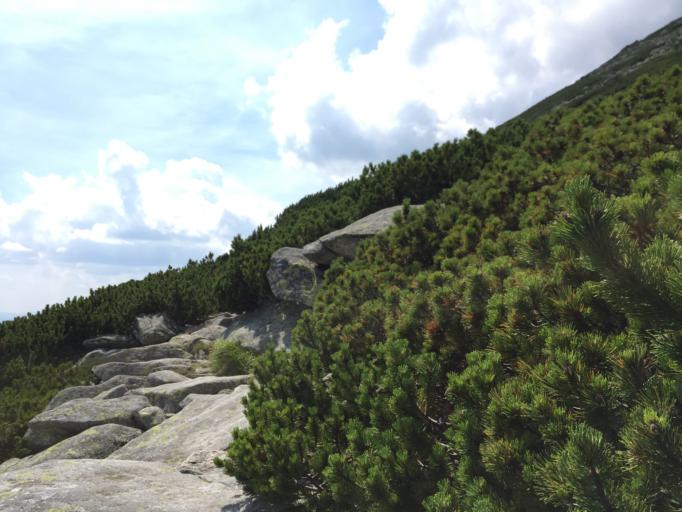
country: SK
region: Presovsky
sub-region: Okres Poprad
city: Vysoke Tatry
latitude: 49.1632
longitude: 20.2118
